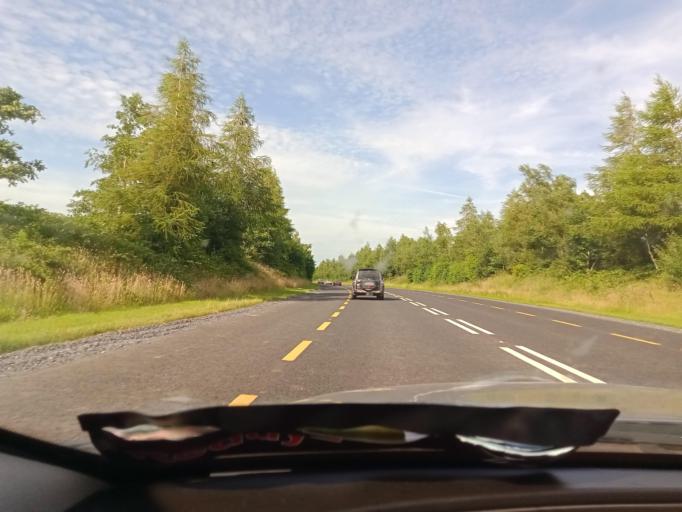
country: IE
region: Leinster
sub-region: An Iarmhi
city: An Muileann gCearr
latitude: 53.4900
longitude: -7.3367
